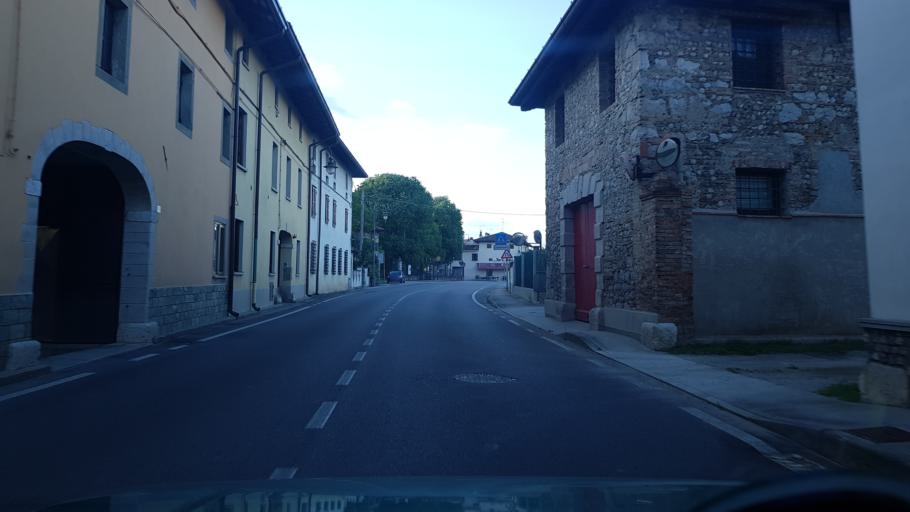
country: IT
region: Friuli Venezia Giulia
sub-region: Provincia di Udine
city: Santa Maria la Longa
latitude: 45.9213
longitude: 13.2947
